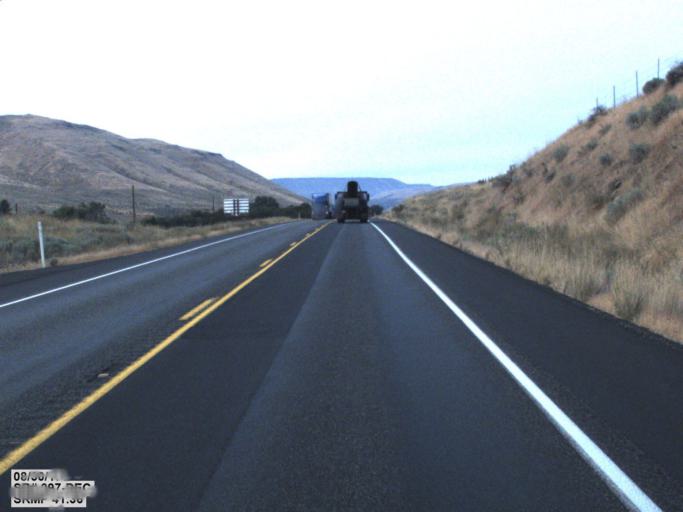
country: US
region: Washington
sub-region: Yakima County
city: Toppenish
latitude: 46.1451
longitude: -120.5143
